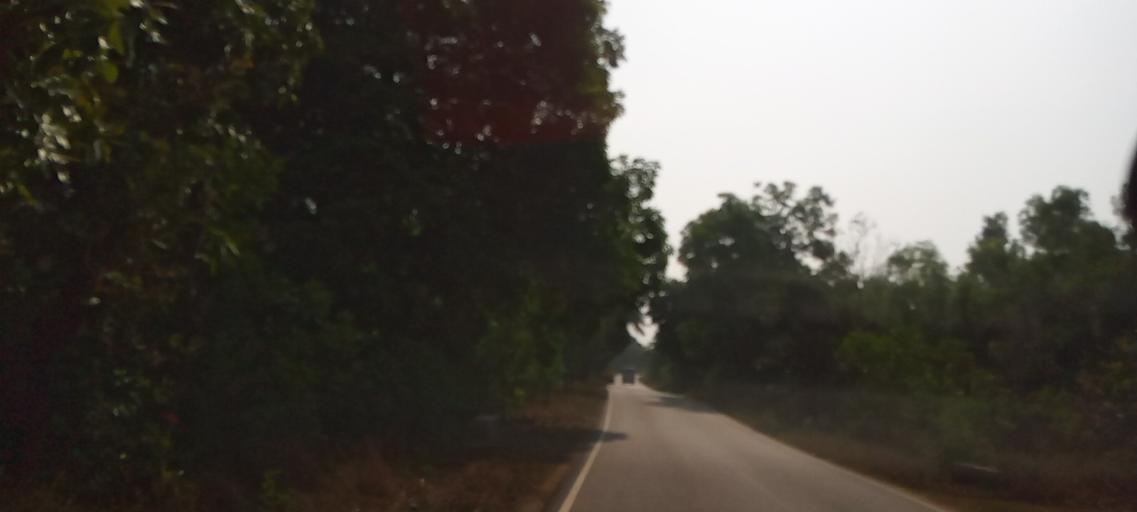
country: IN
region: Karnataka
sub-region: Udupi
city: Coondapoor
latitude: 13.5158
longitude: 74.7915
